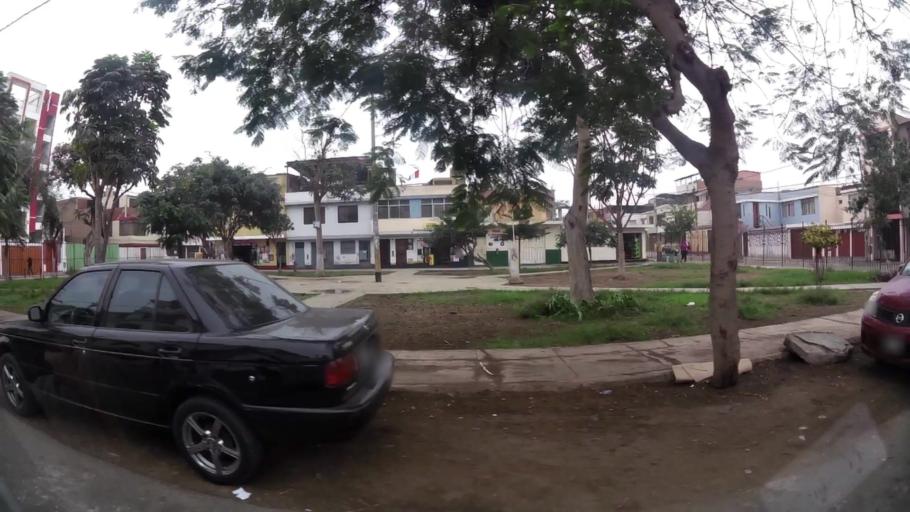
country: PE
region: Lima
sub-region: Lima
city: Surco
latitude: -12.1644
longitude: -76.9776
